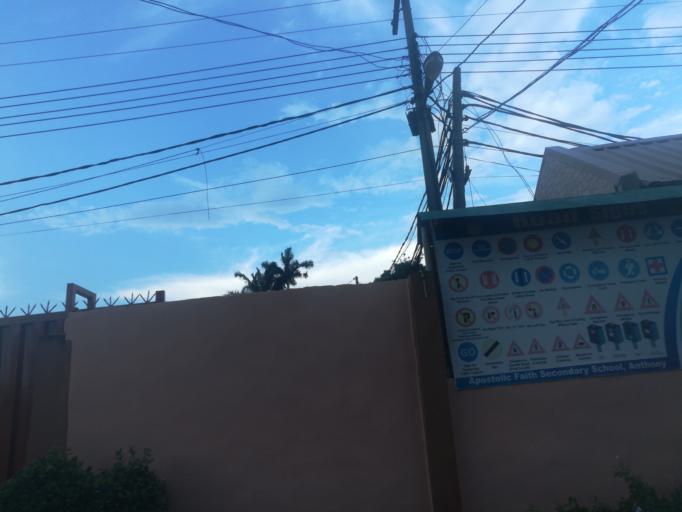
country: NG
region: Lagos
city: Ojota
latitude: 6.5633
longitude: 3.3742
